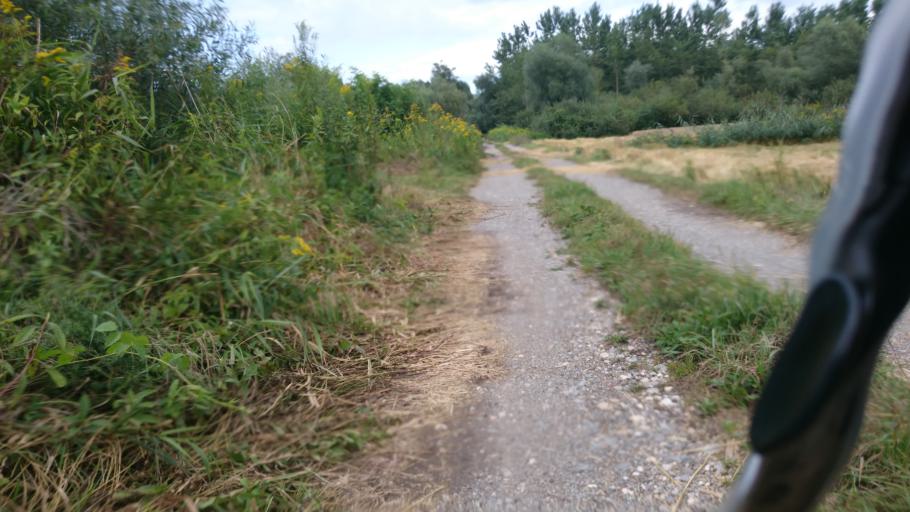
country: SI
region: Brezovica
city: Vnanje Gorice
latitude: 46.0068
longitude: 14.4737
